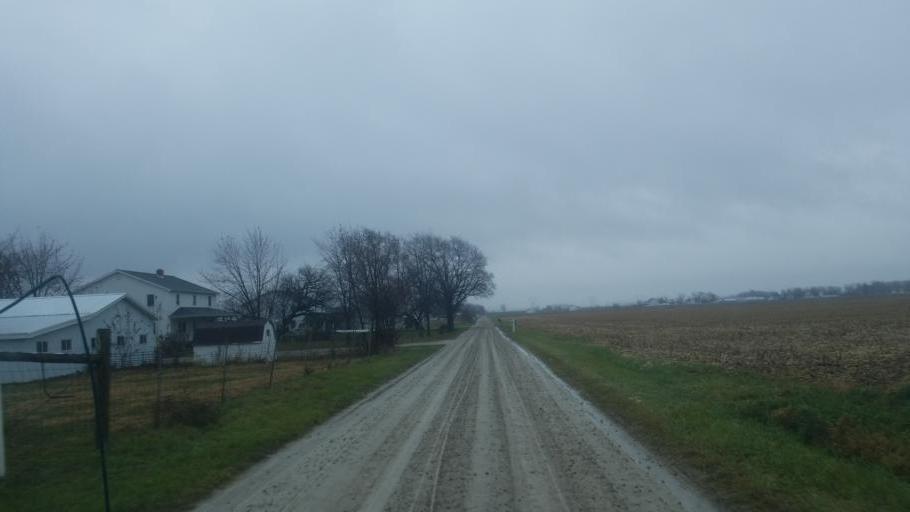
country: US
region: Indiana
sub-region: Adams County
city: Berne
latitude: 40.6515
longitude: -84.8882
